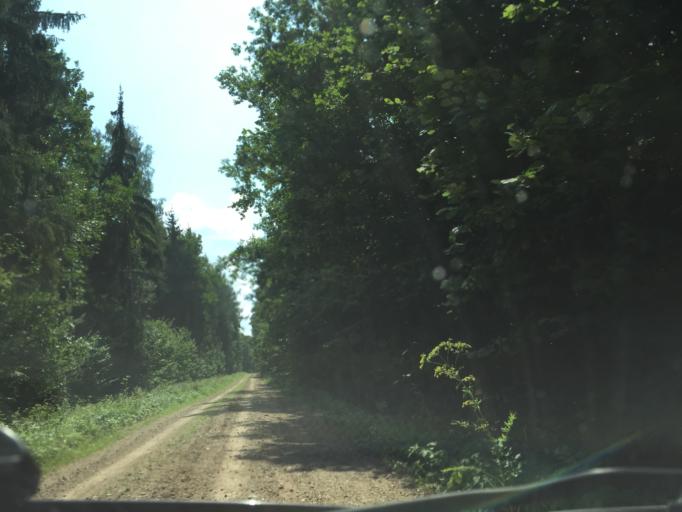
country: LT
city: Zagare
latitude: 56.3932
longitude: 23.2047
